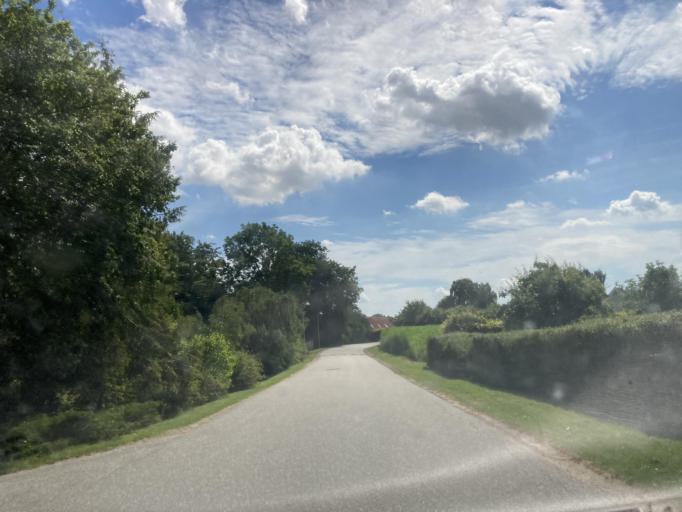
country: DK
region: Zealand
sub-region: Koge Kommune
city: Borup
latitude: 55.4493
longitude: 11.9512
